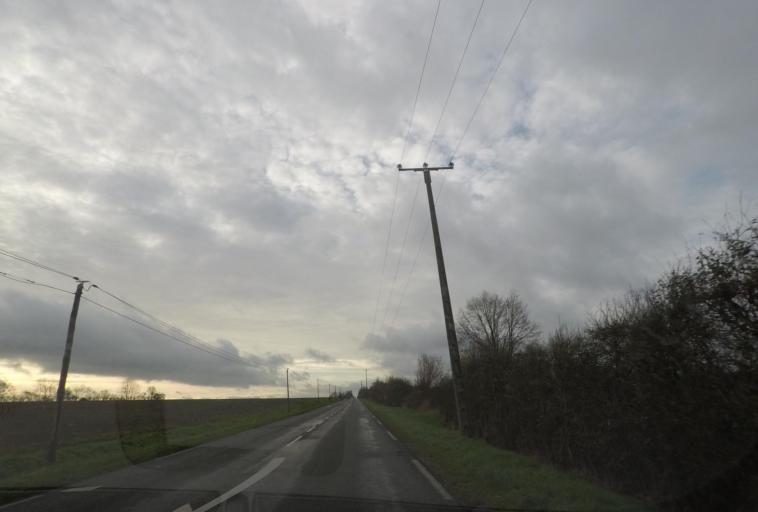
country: FR
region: Pays de la Loire
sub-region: Departement de la Sarthe
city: Saint-Calais
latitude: 47.9545
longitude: 0.7546
